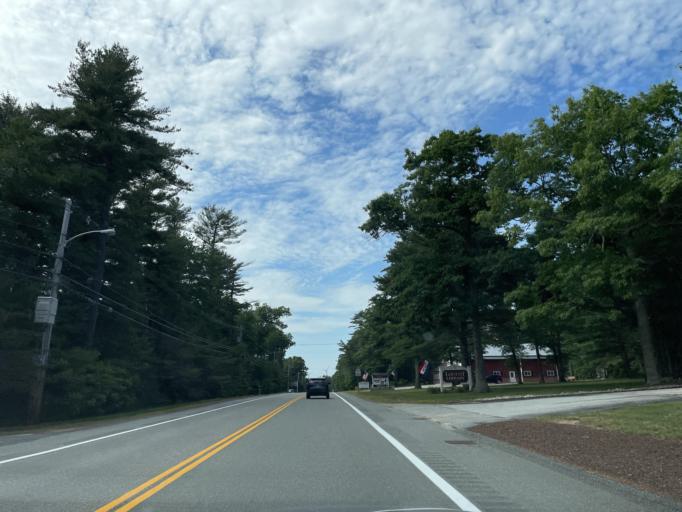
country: US
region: Rhode Island
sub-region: Kent County
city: West Greenwich
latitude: 41.6398
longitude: -71.6888
